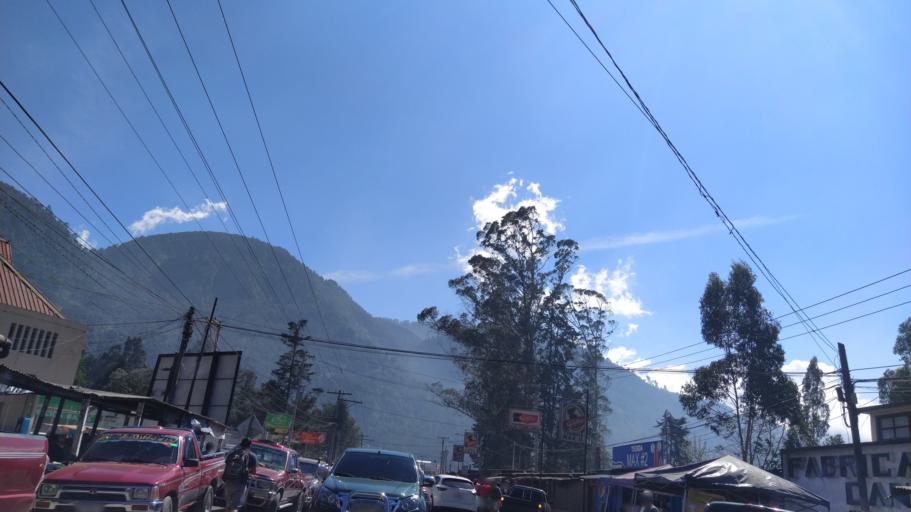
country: GT
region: Quetzaltenango
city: Cantel
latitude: 14.8114
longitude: -91.4482
